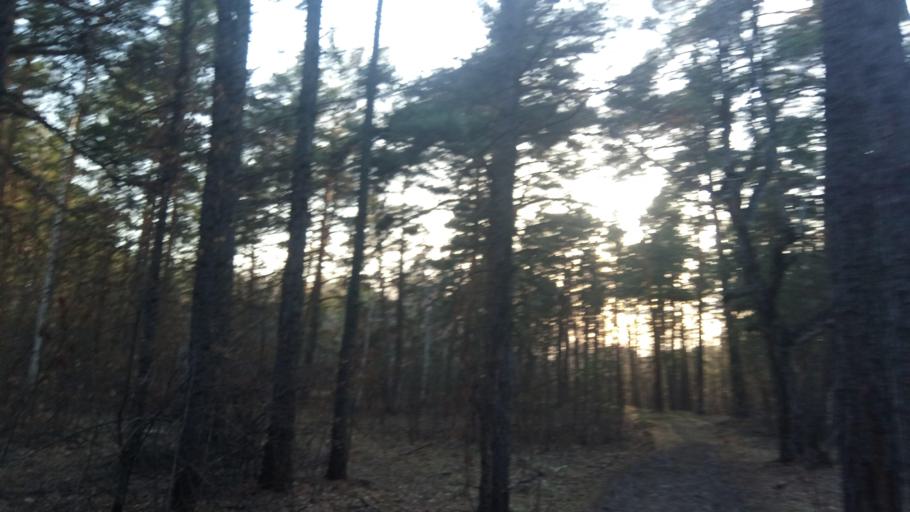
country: RU
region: Chelyabinsk
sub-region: Gorod Chelyabinsk
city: Chelyabinsk
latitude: 55.1565
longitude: 61.3339
